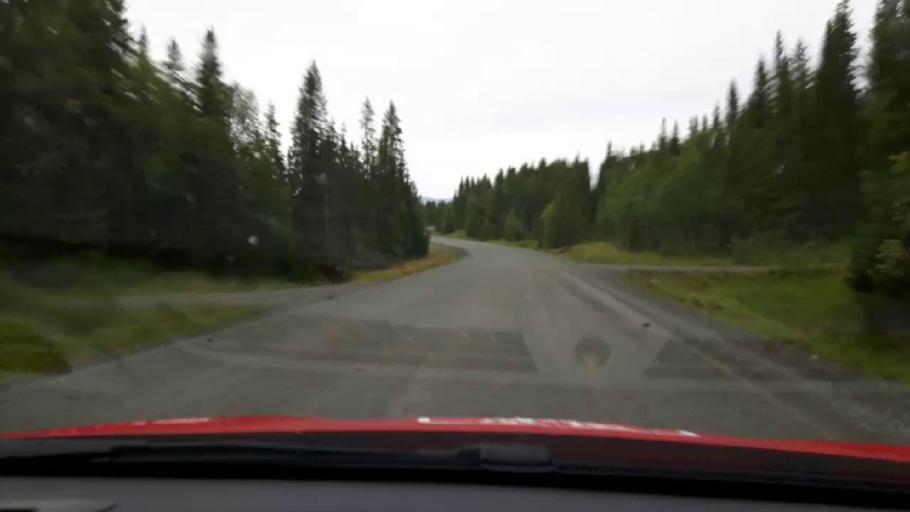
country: SE
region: Jaemtland
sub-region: Are Kommun
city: Are
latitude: 63.4219
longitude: 12.7468
